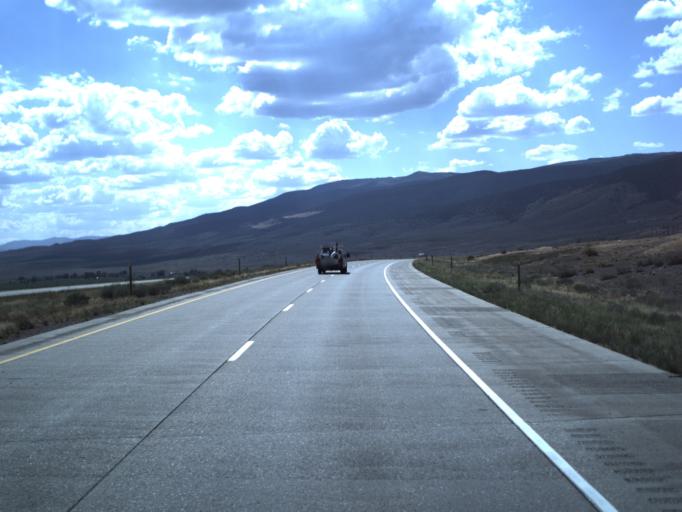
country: US
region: Utah
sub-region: Sevier County
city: Monroe
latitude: 38.6596
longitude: -112.1832
